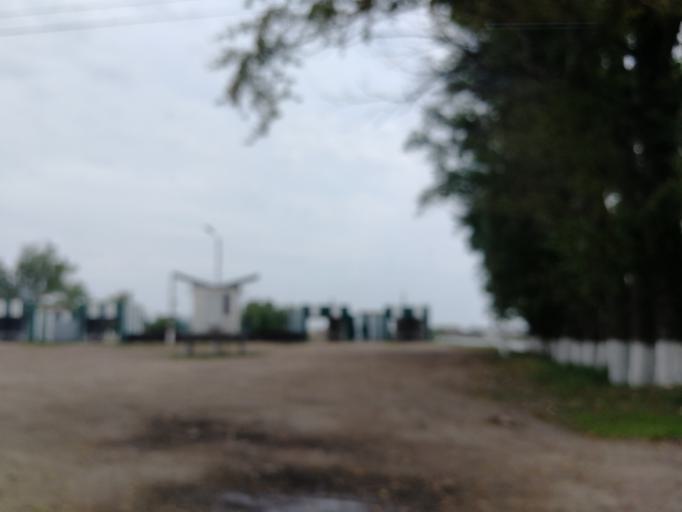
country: RU
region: Tula
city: Tovarkovskiy
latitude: 53.6857
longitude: 38.1922
